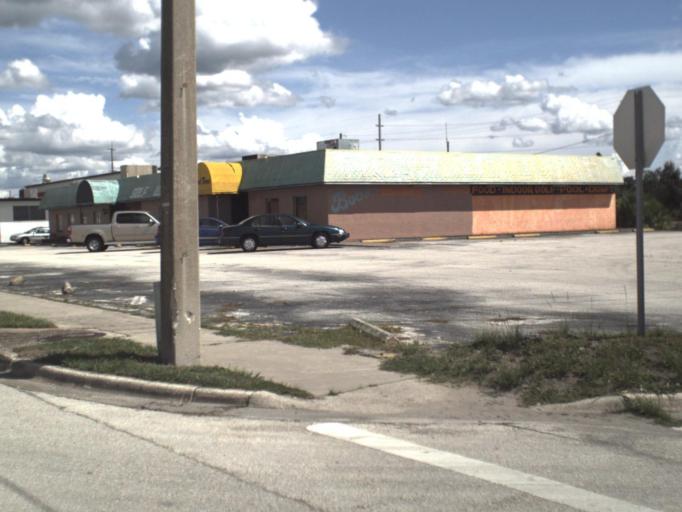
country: US
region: Florida
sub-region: Polk County
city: Mulberry
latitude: 27.8949
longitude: -81.9671
